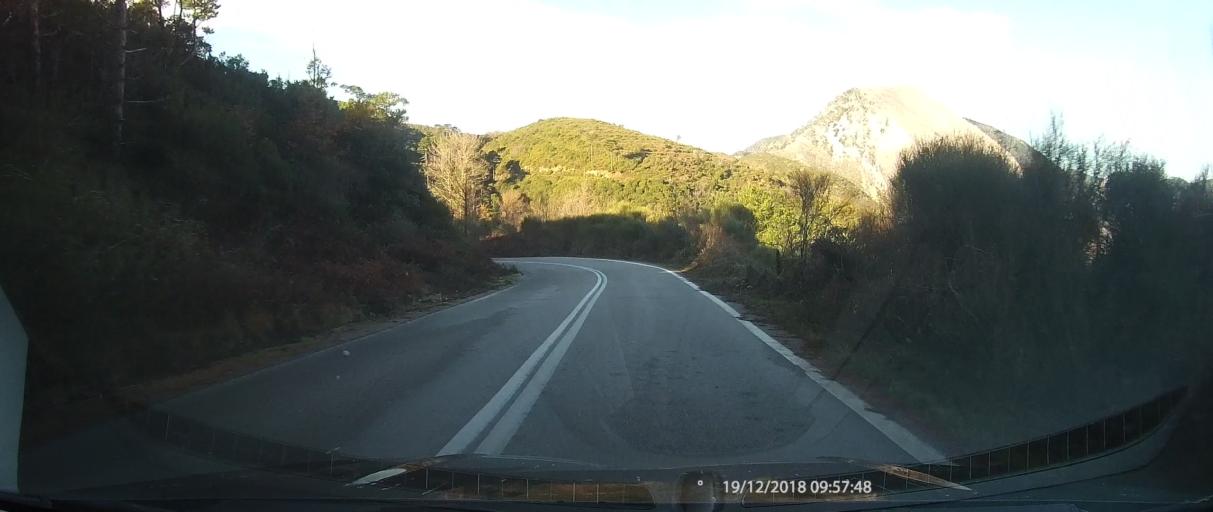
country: GR
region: Peloponnese
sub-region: Nomos Messinias
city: Paralia Vergas
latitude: 37.0879
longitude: 22.2360
